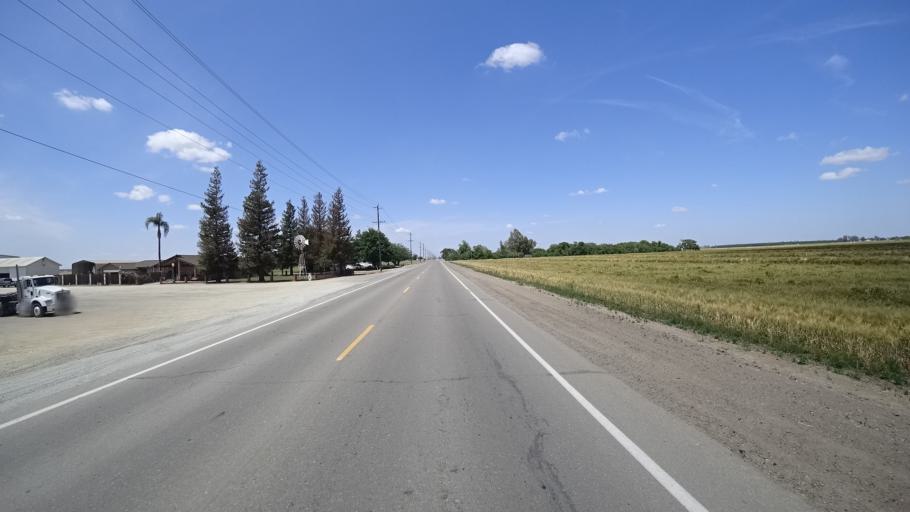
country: US
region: California
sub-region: Kings County
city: Home Garden
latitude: 36.2985
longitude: -119.5670
